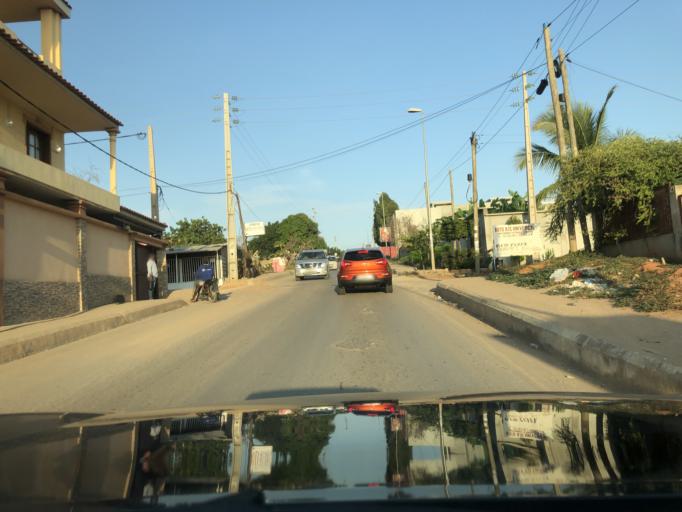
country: AO
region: Luanda
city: Luanda
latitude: -8.9444
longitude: 13.1584
